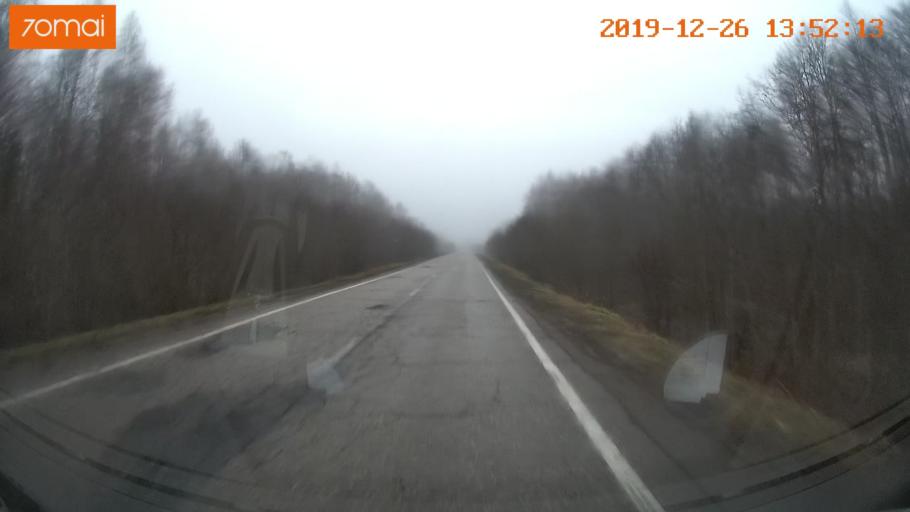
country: RU
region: Jaroslavl
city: Poshekhon'ye
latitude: 58.6346
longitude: 38.5998
